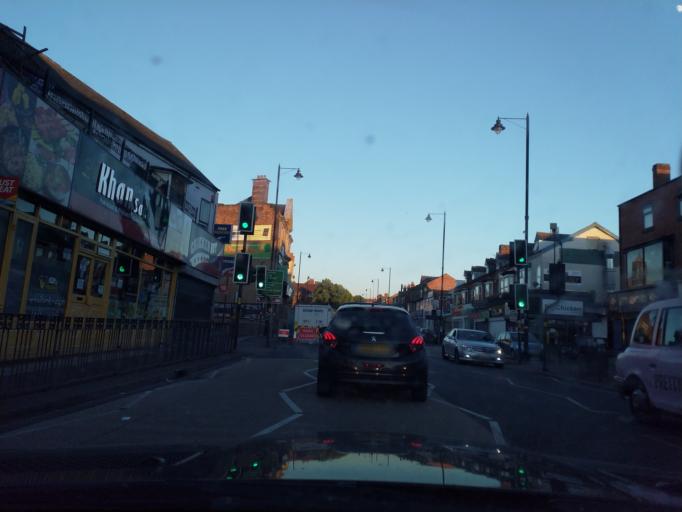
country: GB
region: England
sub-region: City and Borough of Birmingham
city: Birmingham
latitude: 52.4580
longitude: -1.8702
